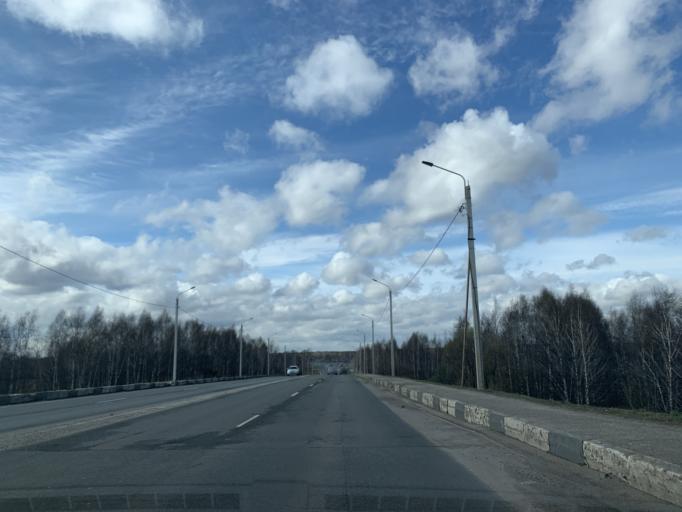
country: RU
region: Jaroslavl
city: Yaroslavl
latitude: 57.6656
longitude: 39.9528
